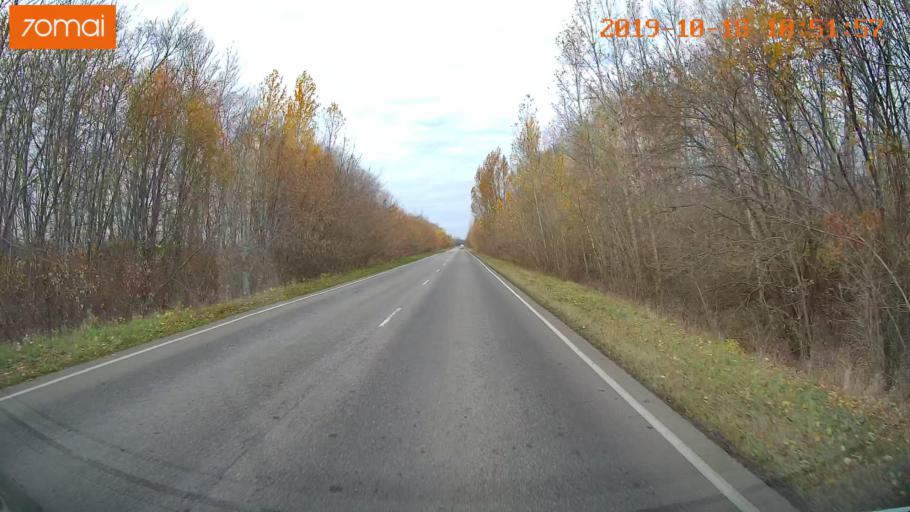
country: RU
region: Tula
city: Yepifan'
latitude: 53.7607
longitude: 38.6595
